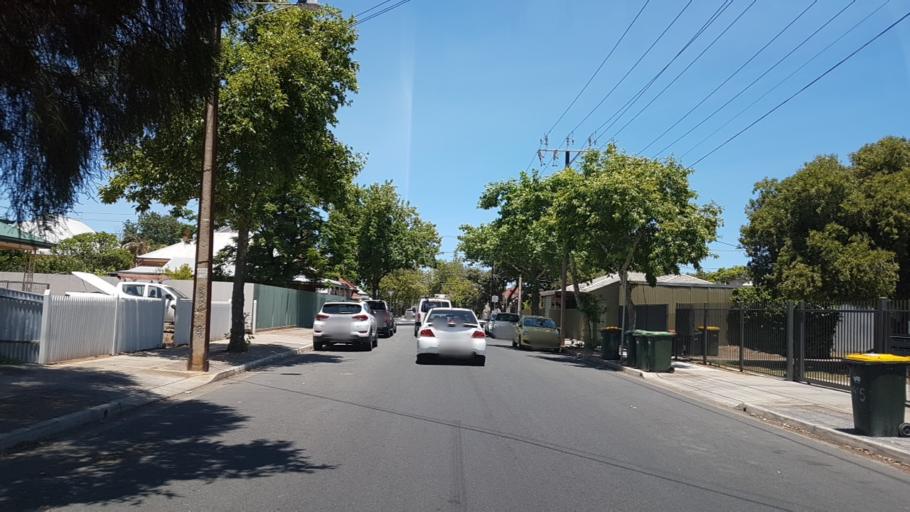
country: AU
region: South Australia
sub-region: City of West Torrens
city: Thebarton
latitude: -34.9214
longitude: 138.5622
